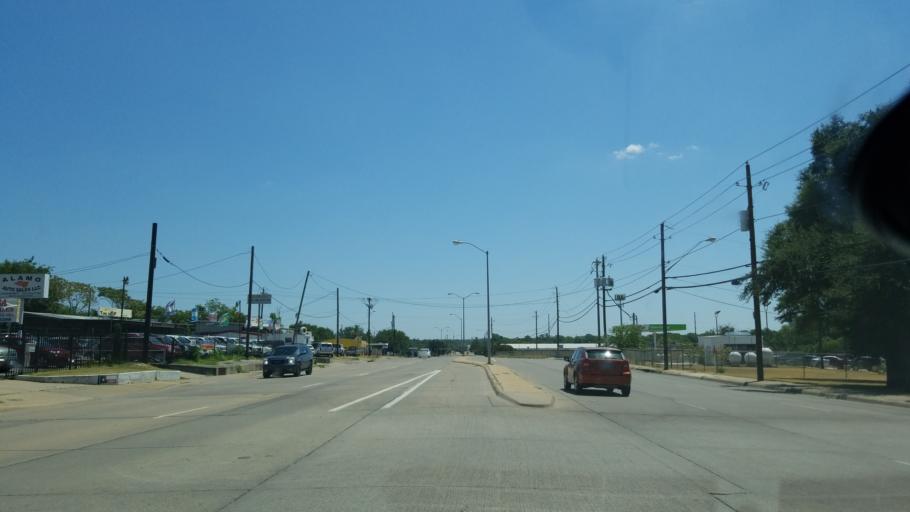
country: US
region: Texas
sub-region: Dallas County
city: Cockrell Hill
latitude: 32.7245
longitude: -96.8916
